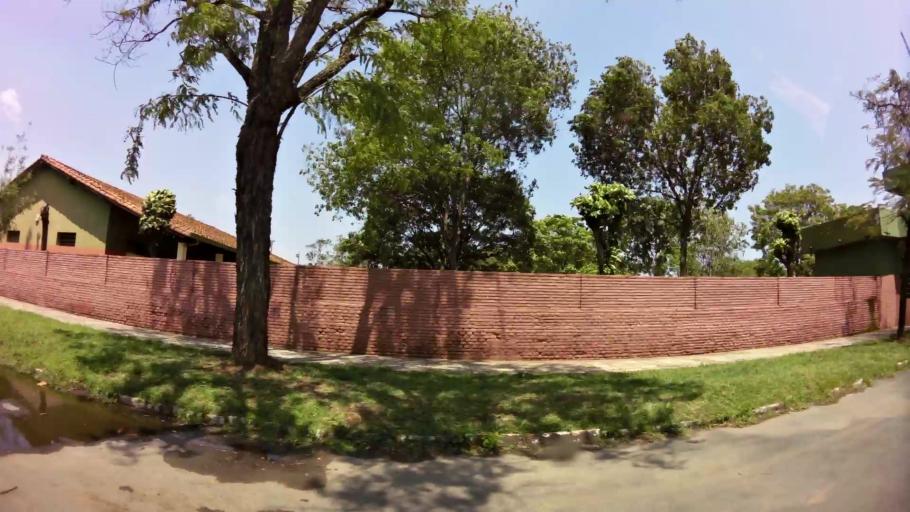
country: PY
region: Asuncion
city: Asuncion
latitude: -25.3051
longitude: -57.6522
